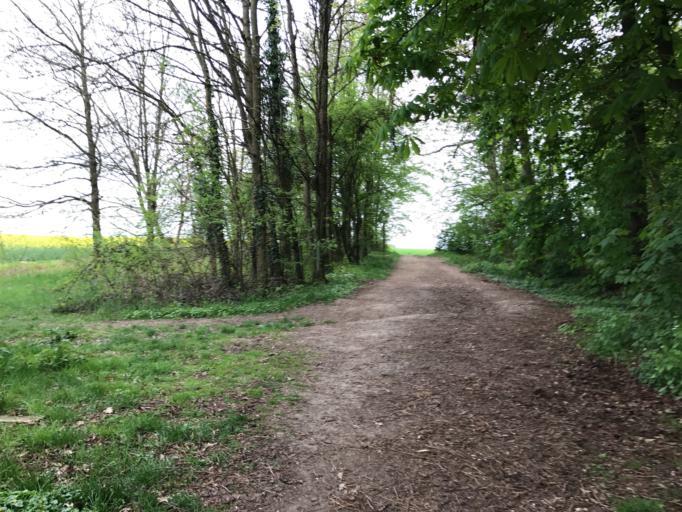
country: DE
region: Rheinland-Pfalz
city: Ober-Olm
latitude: 49.9504
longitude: 8.1804
